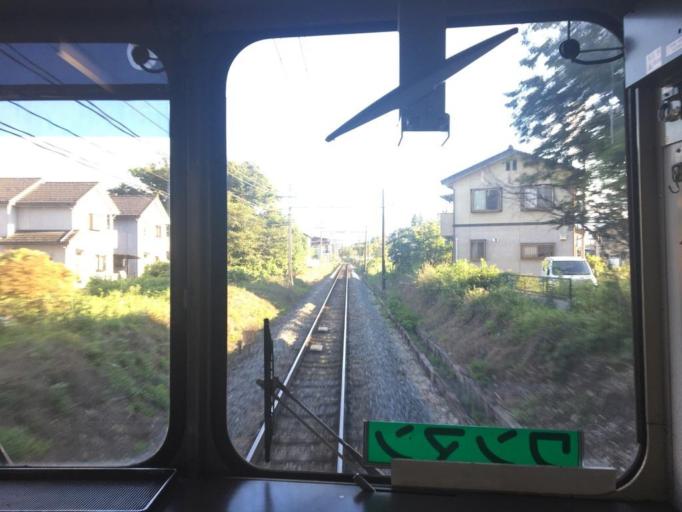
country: JP
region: Saitama
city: Chichibu
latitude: 36.0362
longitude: 139.0984
